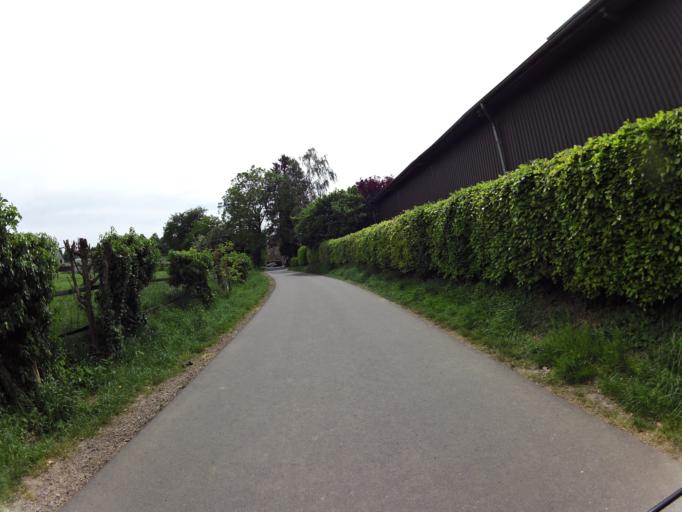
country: DE
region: North Rhine-Westphalia
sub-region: Regierungsbezirk Koln
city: Wurselen
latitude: 50.8285
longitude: 6.1392
